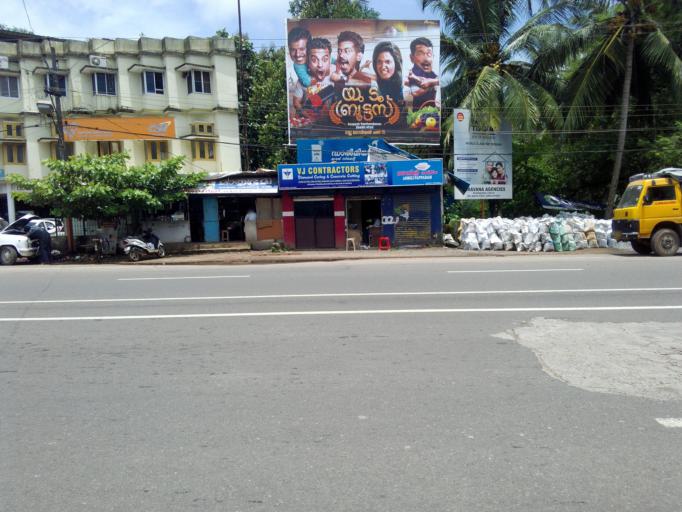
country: IN
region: Kerala
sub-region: Kozhikode
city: Kozhikode
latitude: 11.2814
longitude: 75.7877
